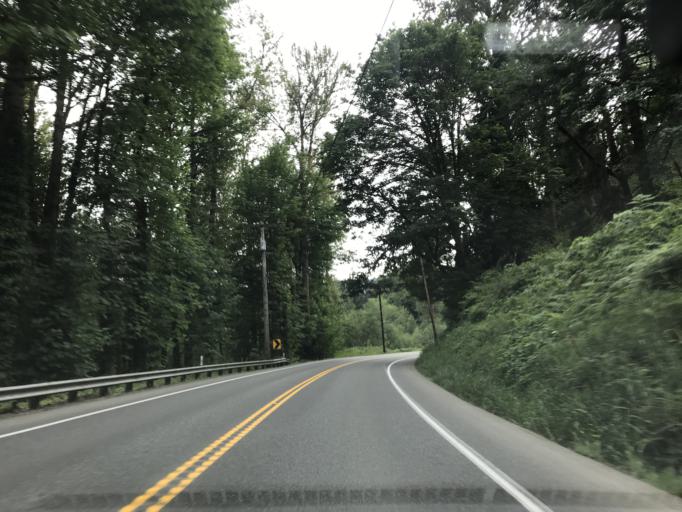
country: US
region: Washington
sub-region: King County
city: Fall City
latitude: 47.5335
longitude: -121.9163
